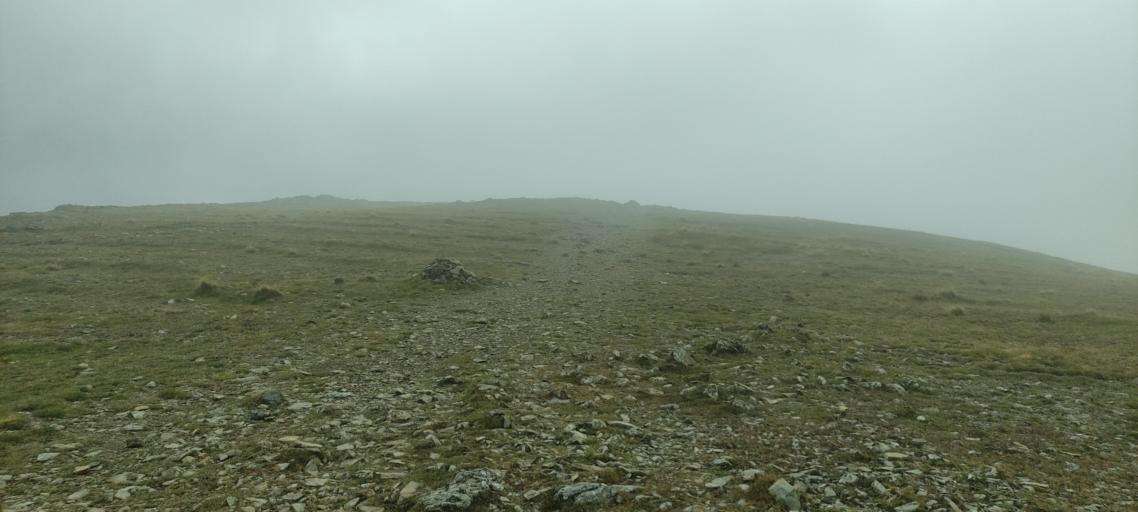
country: GB
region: England
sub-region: Cumbria
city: Ambleside
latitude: 54.5142
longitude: -2.9751
